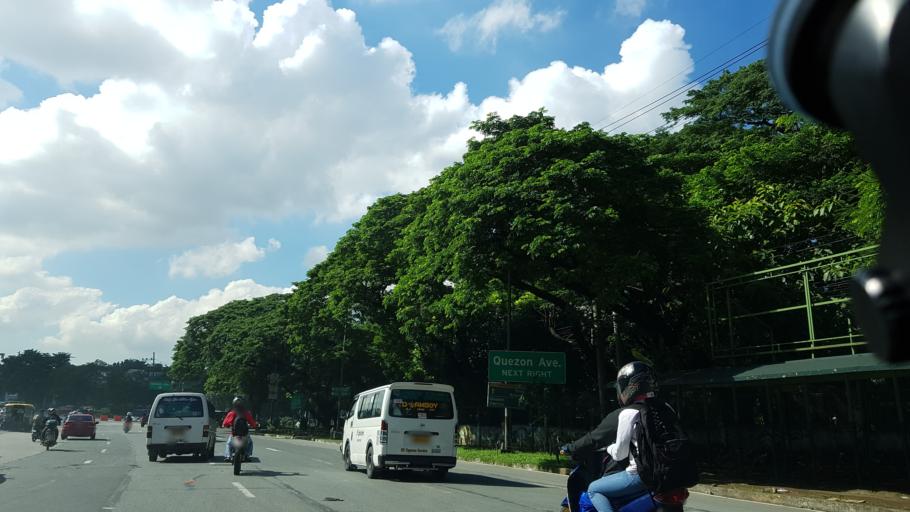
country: PH
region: Metro Manila
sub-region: Quezon City
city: Quezon City
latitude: 14.6513
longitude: 121.0465
